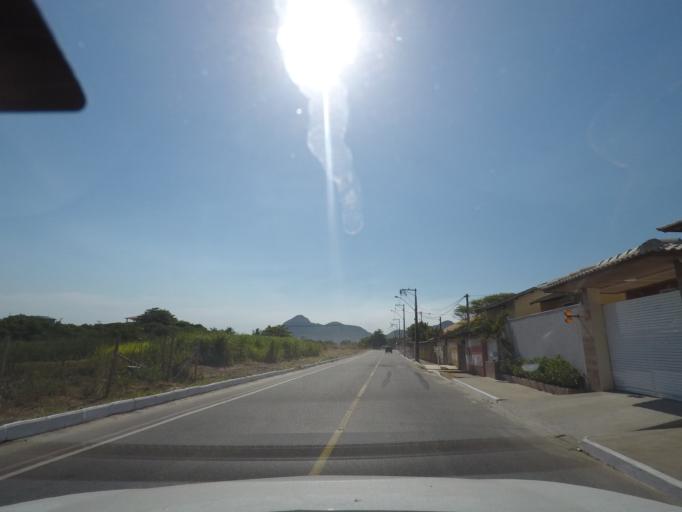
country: BR
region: Rio de Janeiro
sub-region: Niteroi
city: Niteroi
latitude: -22.9675
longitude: -42.9721
